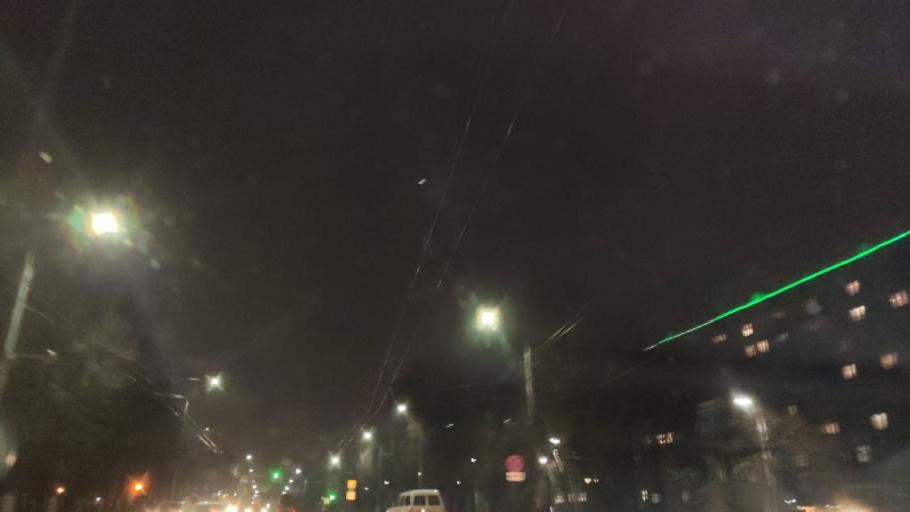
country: RU
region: Moskovskaya
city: Dubrovitsy
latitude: 55.4248
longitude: 37.5056
